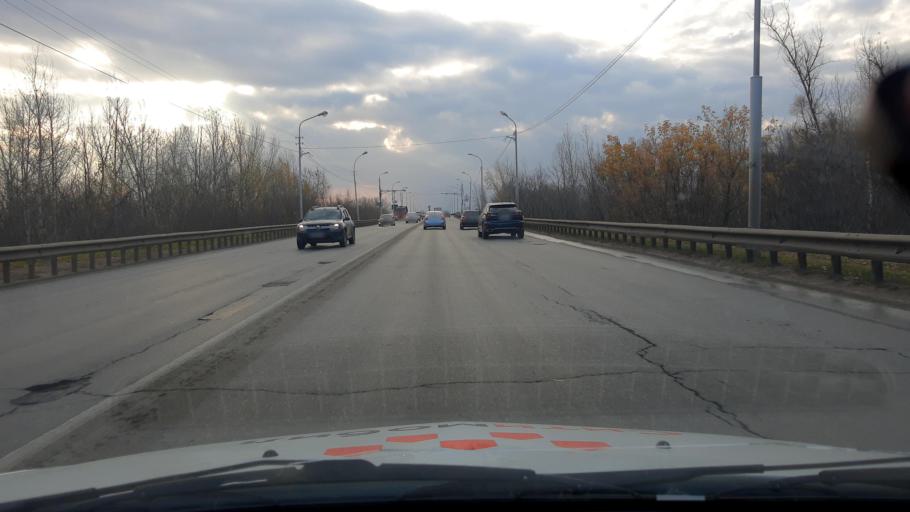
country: RU
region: Bashkortostan
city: Iglino
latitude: 54.7909
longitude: 56.2136
